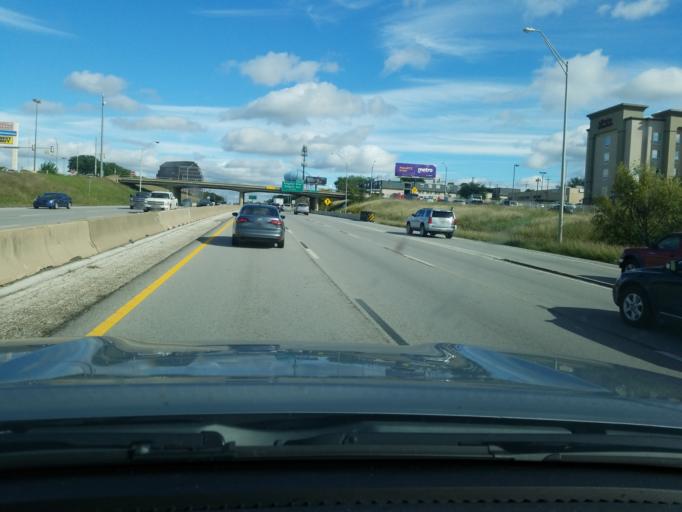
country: US
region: Texas
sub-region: Tarrant County
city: White Settlement
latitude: 32.7357
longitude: -97.4359
